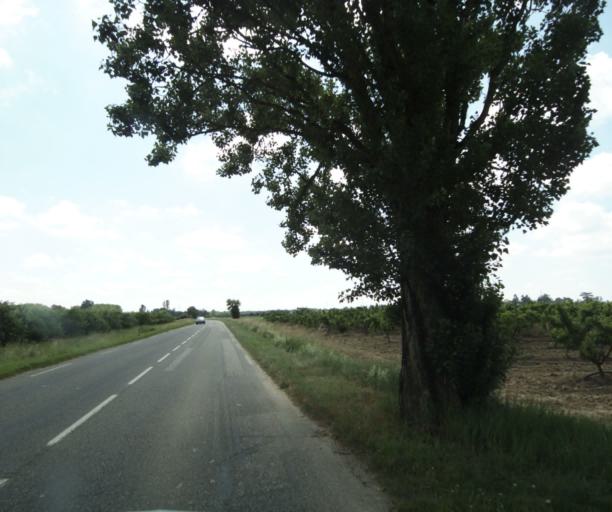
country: FR
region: Midi-Pyrenees
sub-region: Departement du Tarn-et-Garonne
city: Montauban
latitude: 44.0659
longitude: 1.3566
